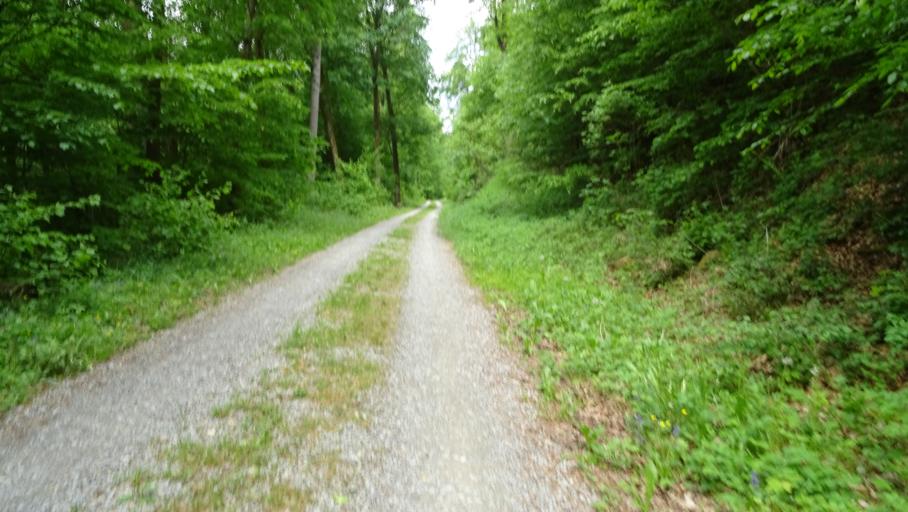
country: DE
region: Baden-Wuerttemberg
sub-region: Karlsruhe Region
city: Neckargerach
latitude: 49.4109
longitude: 9.0948
